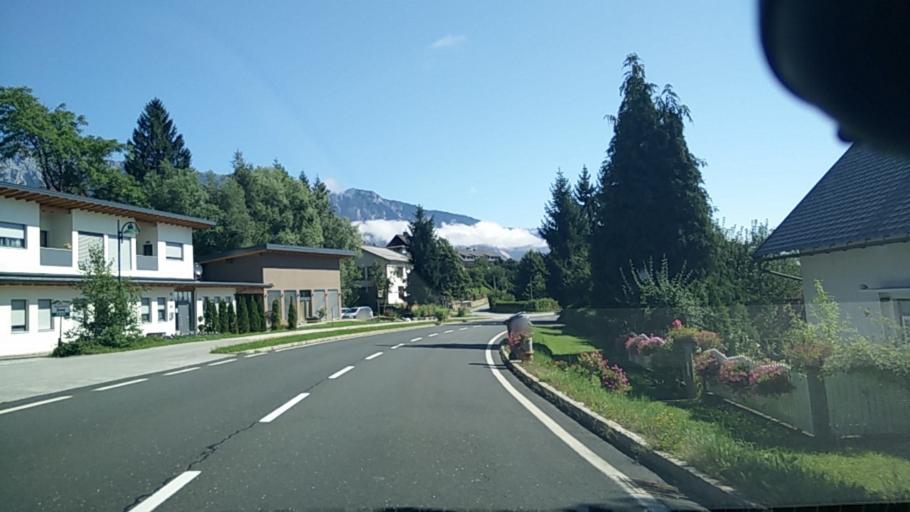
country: AT
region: Carinthia
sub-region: Politischer Bezirk Villach Land
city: Hohenthurn
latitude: 46.5414
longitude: 13.6453
